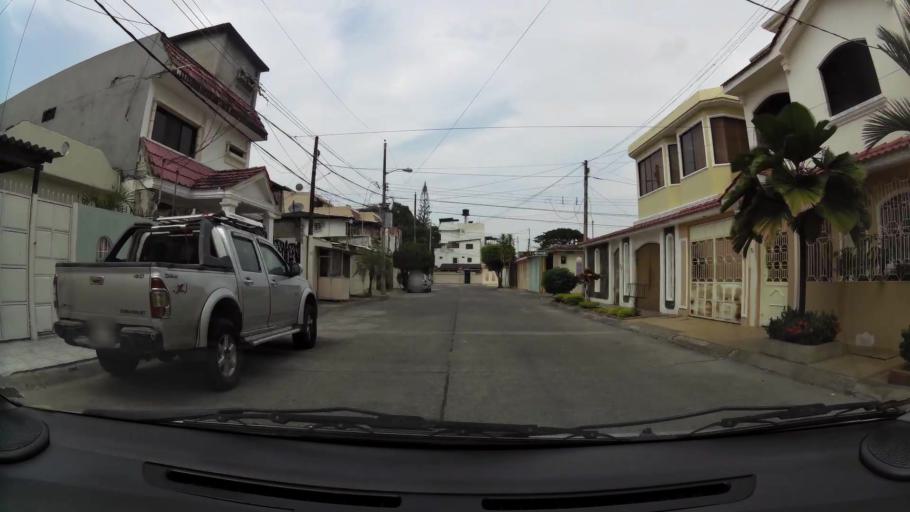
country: EC
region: Guayas
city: Eloy Alfaro
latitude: -2.1150
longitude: -79.8902
